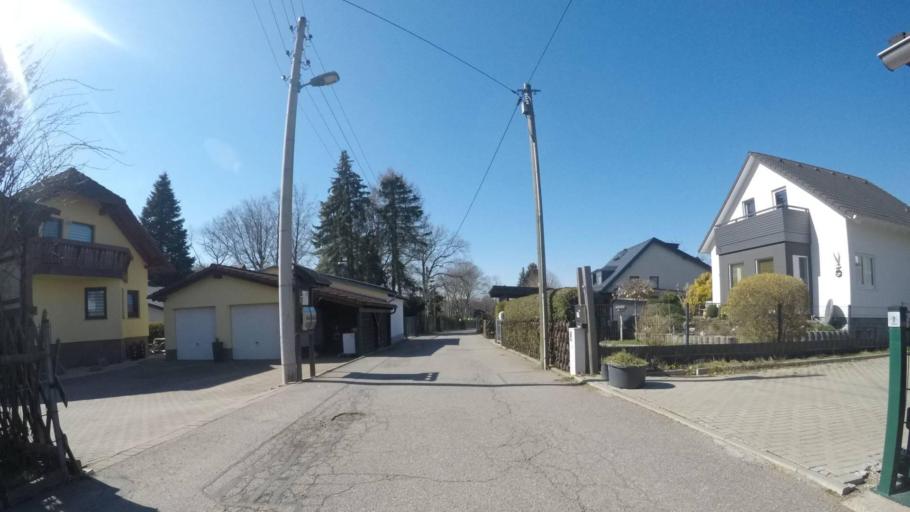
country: DE
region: Saxony
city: Limbach-Oberfrohna
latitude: 50.8688
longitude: 12.7822
